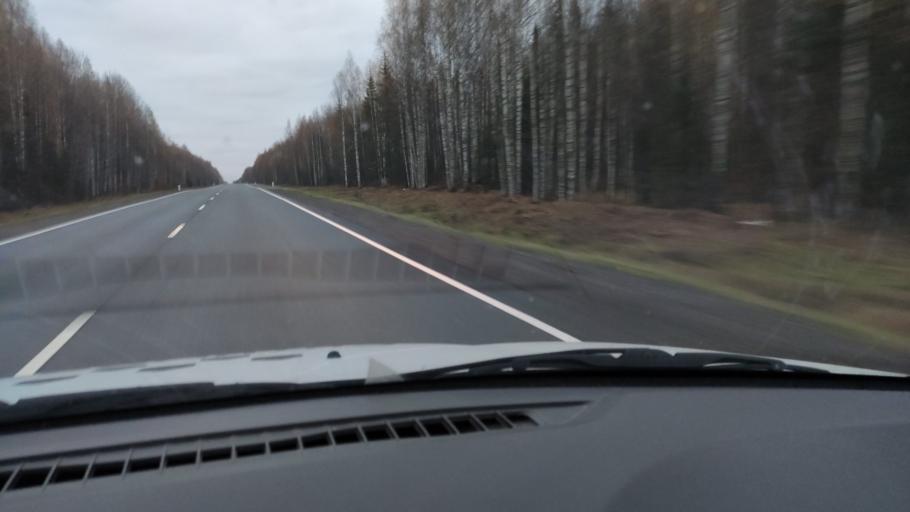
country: RU
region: Kirov
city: Kostino
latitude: 58.8226
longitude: 52.9773
